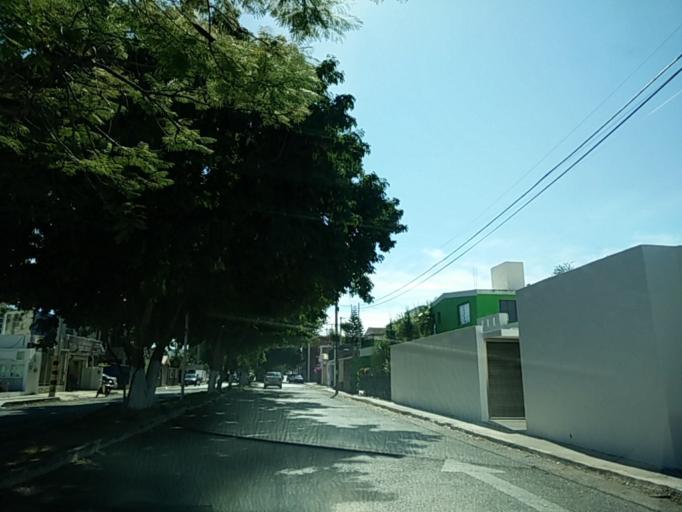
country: MX
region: Yucatan
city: Merida
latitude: 20.9997
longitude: -89.6057
